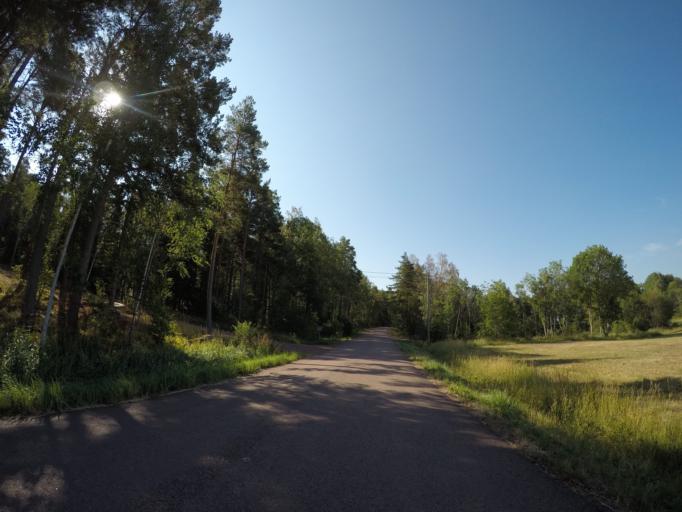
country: AX
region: Alands landsbygd
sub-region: Finstroem
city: Finstroem
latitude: 60.3327
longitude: 19.9112
